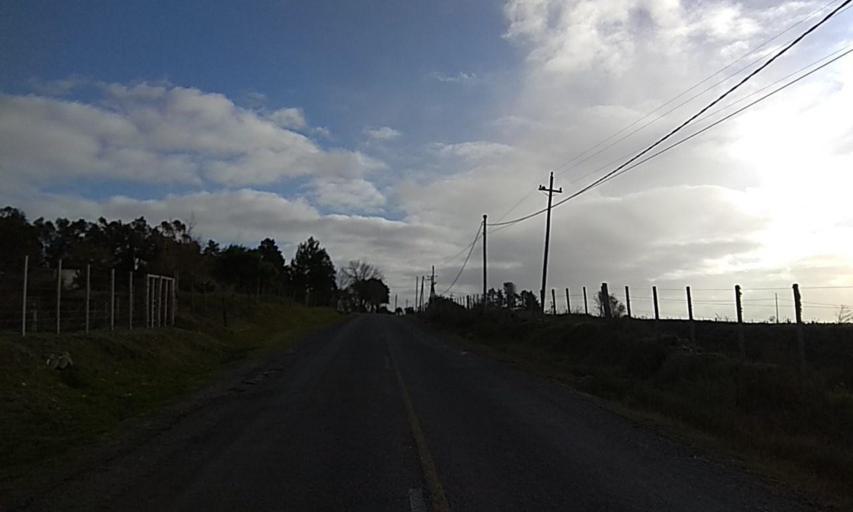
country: UY
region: Florida
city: Florida
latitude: -34.0462
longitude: -56.1890
